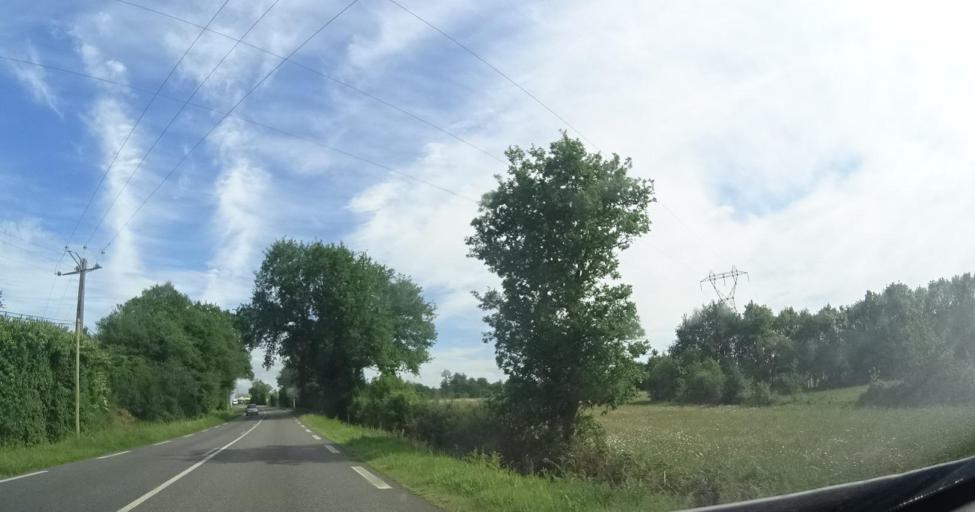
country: FR
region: Pays de la Loire
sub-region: Departement de la Loire-Atlantique
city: Fegreac
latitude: 47.5909
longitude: -2.0081
